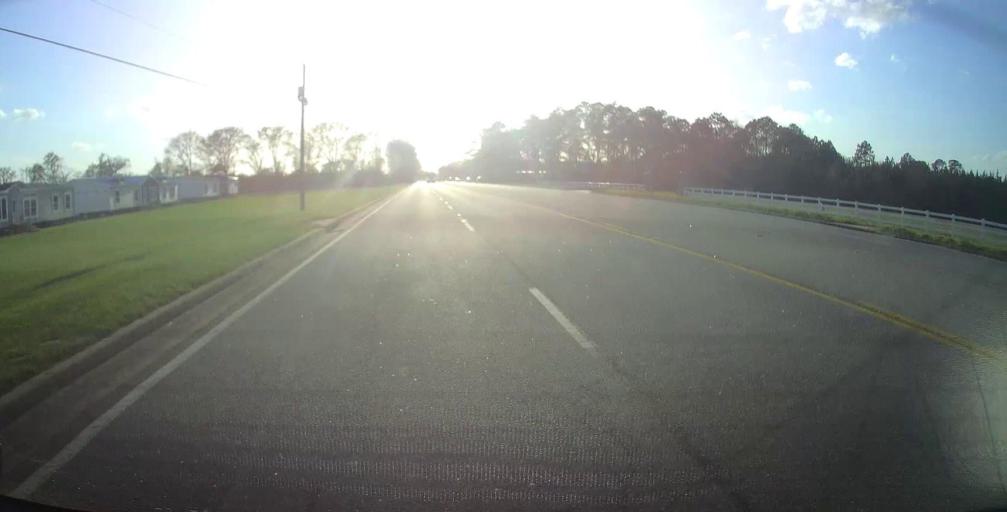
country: US
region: Georgia
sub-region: Evans County
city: Claxton
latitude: 32.1568
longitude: -81.9404
